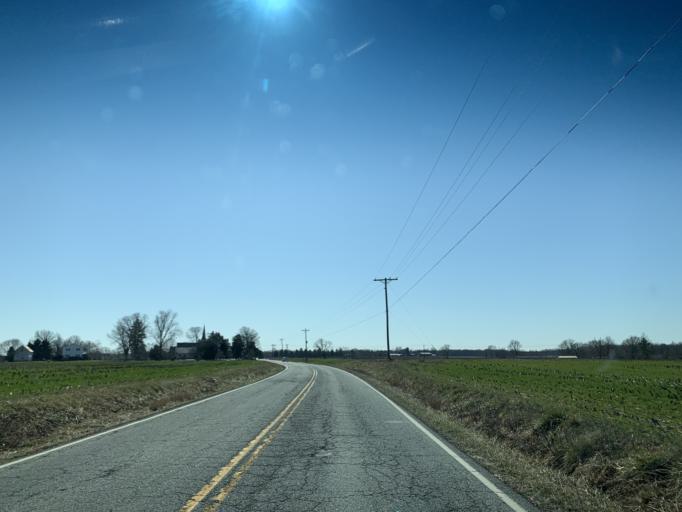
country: US
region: Maryland
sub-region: Cecil County
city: Charlestown
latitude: 39.4290
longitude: -75.9165
